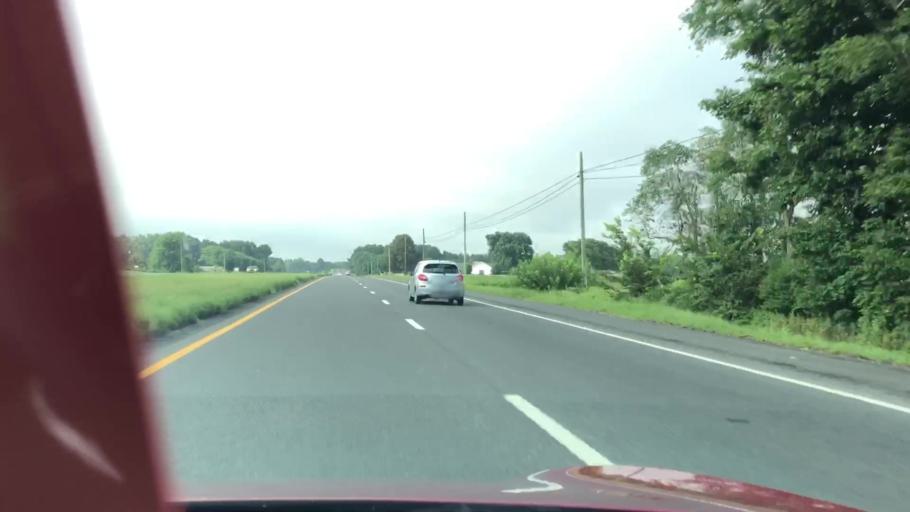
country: US
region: Delaware
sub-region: Sussex County
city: Bridgeville
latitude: 38.8286
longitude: -75.5837
